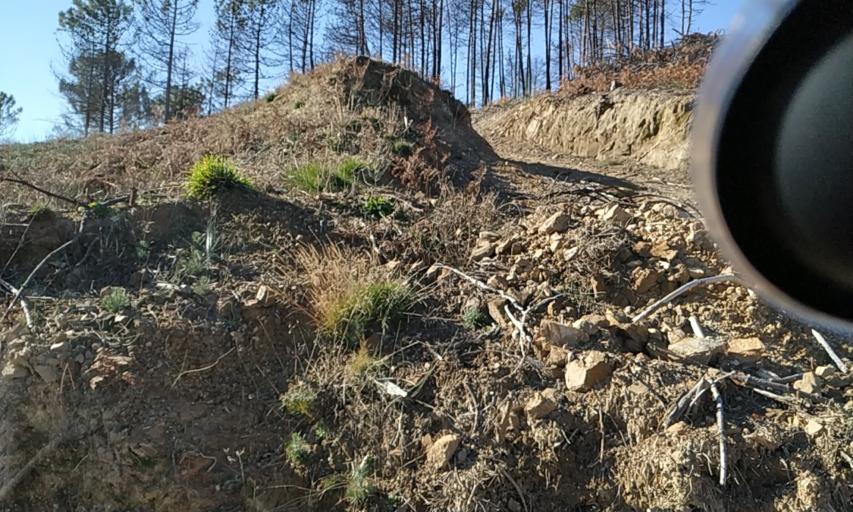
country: PT
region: Vila Real
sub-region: Vila Real
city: Vila Real
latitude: 41.3322
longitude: -7.7568
